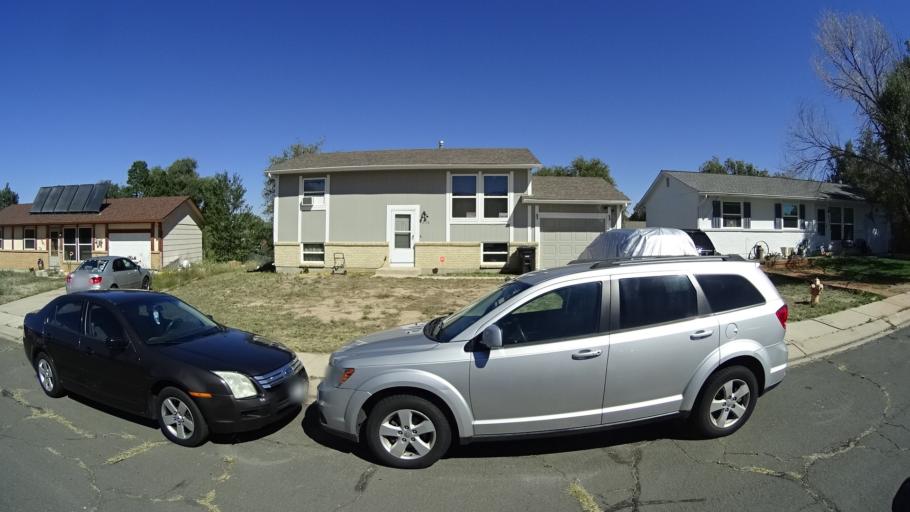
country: US
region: Colorado
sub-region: El Paso County
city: Stratmoor
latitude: 38.8107
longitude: -104.7381
